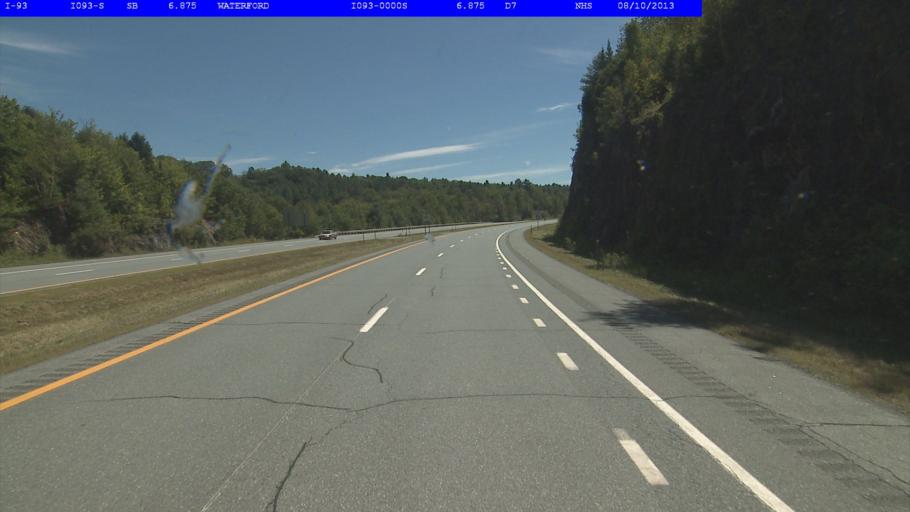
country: US
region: Vermont
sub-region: Caledonia County
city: St Johnsbury
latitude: 44.4276
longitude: -71.9439
